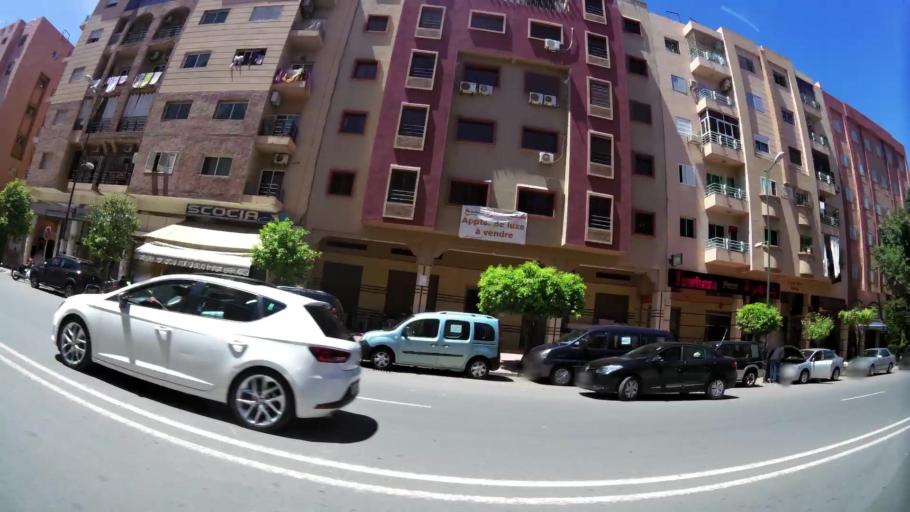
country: MA
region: Marrakech-Tensift-Al Haouz
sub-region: Marrakech
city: Marrakesh
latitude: 31.6356
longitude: -8.0577
